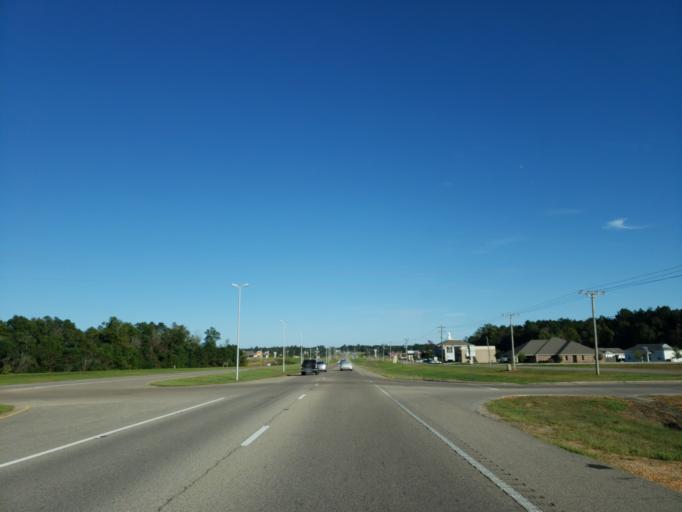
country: US
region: Mississippi
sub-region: Forrest County
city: Petal
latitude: 31.3519
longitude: -89.2441
